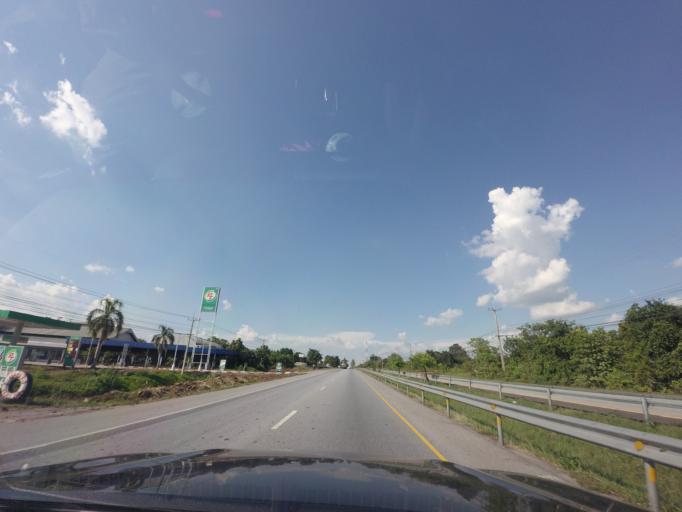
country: TH
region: Nakhon Ratchasima
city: Sida
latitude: 15.5309
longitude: 102.5440
